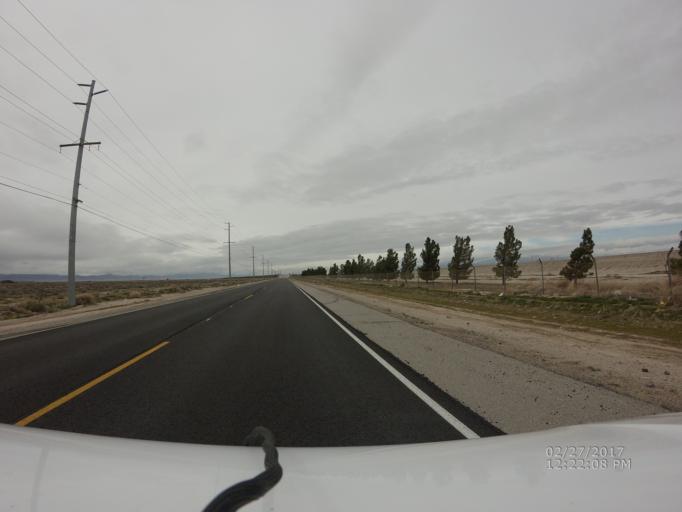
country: US
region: California
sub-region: Los Angeles County
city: Lancaster
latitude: 34.7770
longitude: -118.1623
